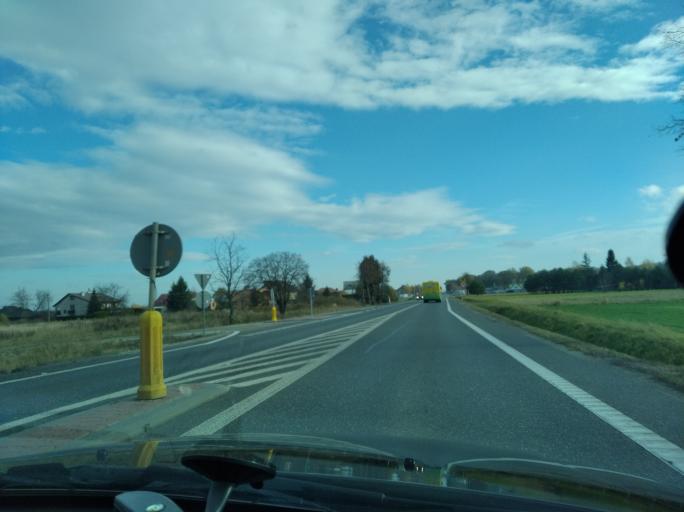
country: PL
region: Subcarpathian Voivodeship
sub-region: Powiat debicki
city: Brzeznica
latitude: 50.0582
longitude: 21.4673
